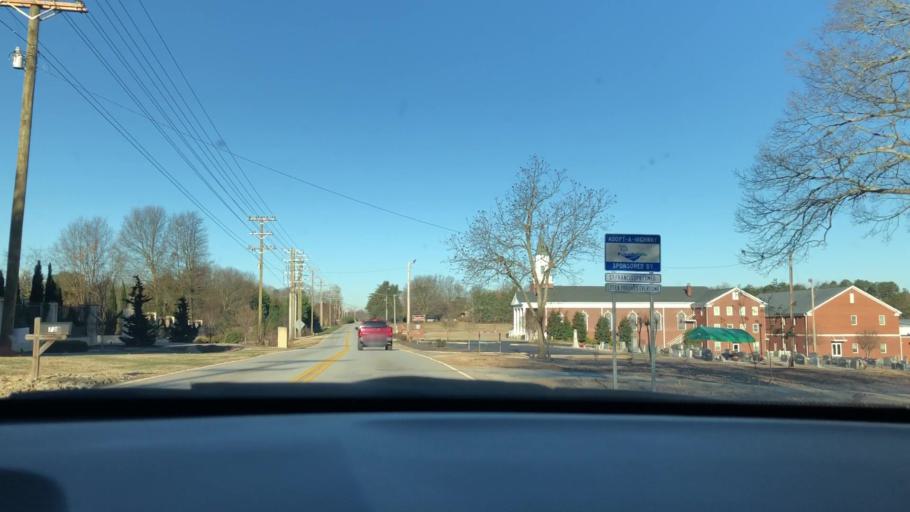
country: US
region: South Carolina
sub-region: Greenville County
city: Five Forks
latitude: 34.8182
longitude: -82.2056
